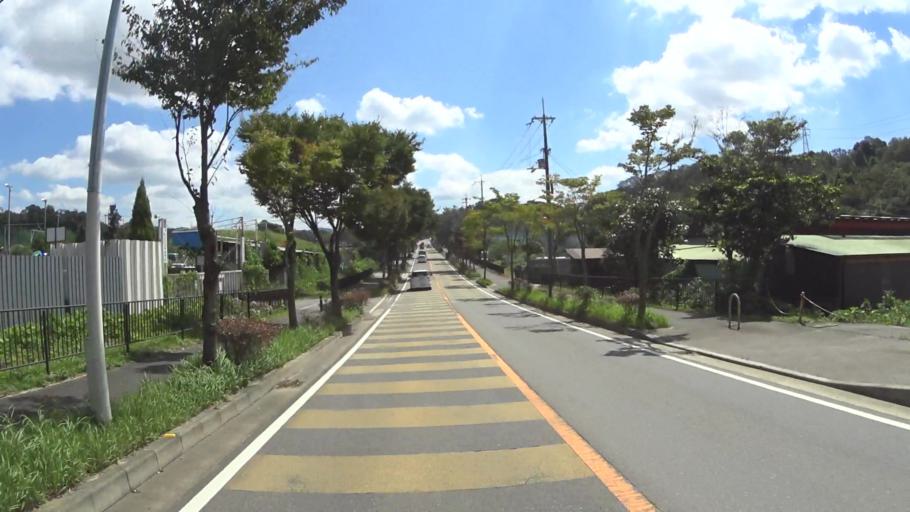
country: JP
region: Kyoto
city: Uji
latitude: 34.8631
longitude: 135.7974
